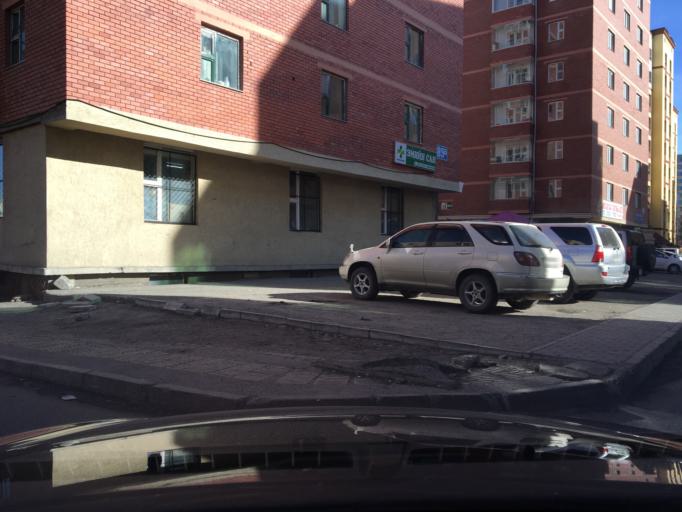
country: MN
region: Ulaanbaatar
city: Ulaanbaatar
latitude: 47.8912
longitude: 106.8963
